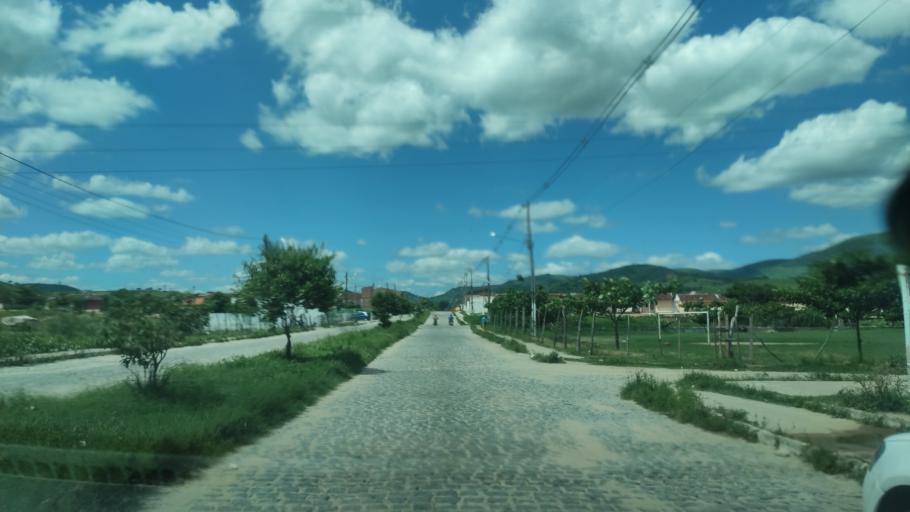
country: BR
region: Alagoas
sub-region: Uniao Dos Palmares
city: Uniao dos Palmares
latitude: -9.1501
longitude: -36.0081
